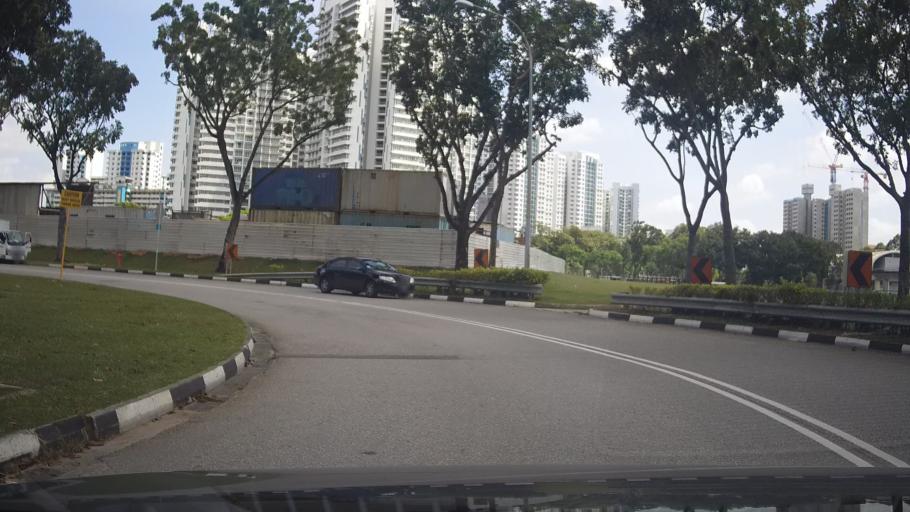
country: SG
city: Singapore
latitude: 1.3107
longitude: 103.8681
